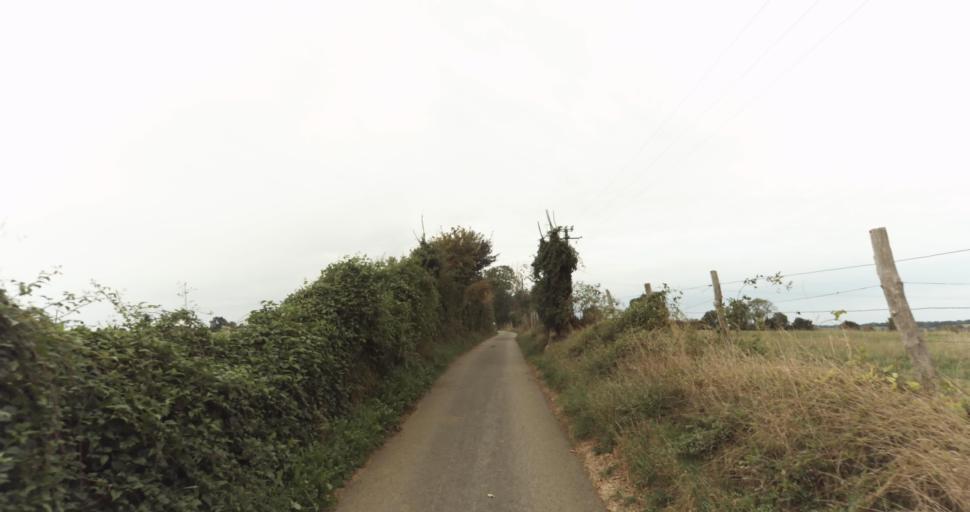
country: FR
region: Lower Normandy
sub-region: Departement de l'Orne
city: Gace
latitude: 48.7629
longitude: 0.3234
